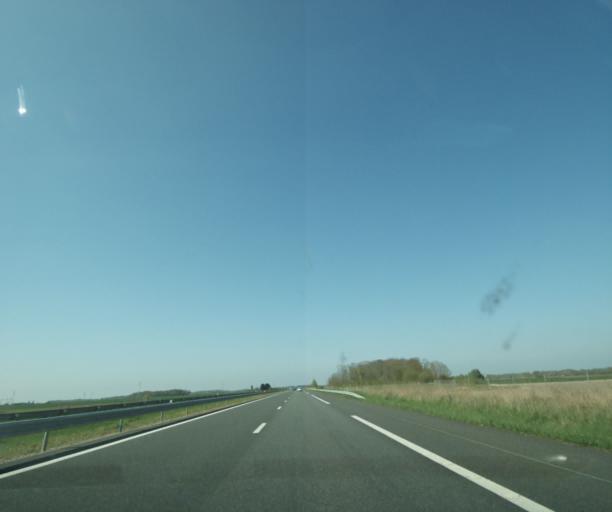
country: FR
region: Centre
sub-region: Departement du Loiret
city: Changy-les-Bois
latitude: 47.8798
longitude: 2.6894
